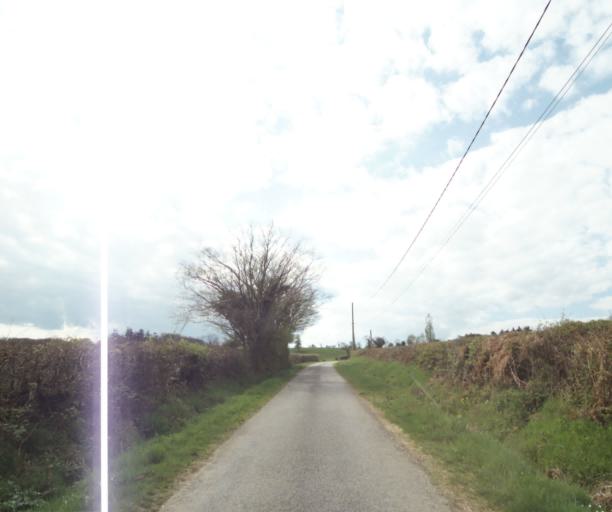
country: FR
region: Bourgogne
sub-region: Departement de Saone-et-Loire
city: Ciry-le-Noble
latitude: 46.5500
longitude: 4.3130
